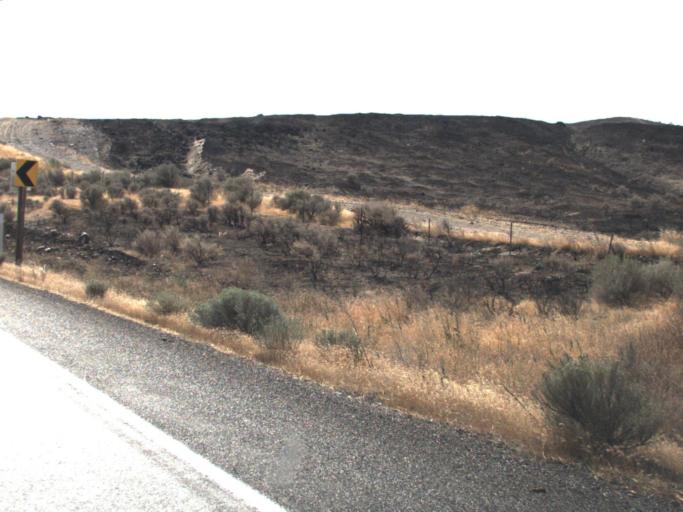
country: US
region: Washington
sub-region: Grant County
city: Desert Aire
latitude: 46.6074
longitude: -119.7366
